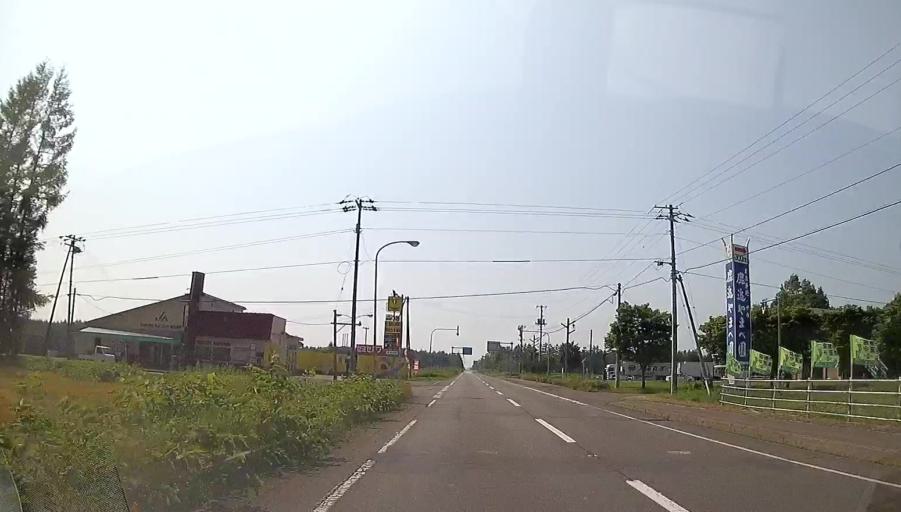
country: JP
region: Hokkaido
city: Otofuke
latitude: 43.1702
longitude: 143.1114
